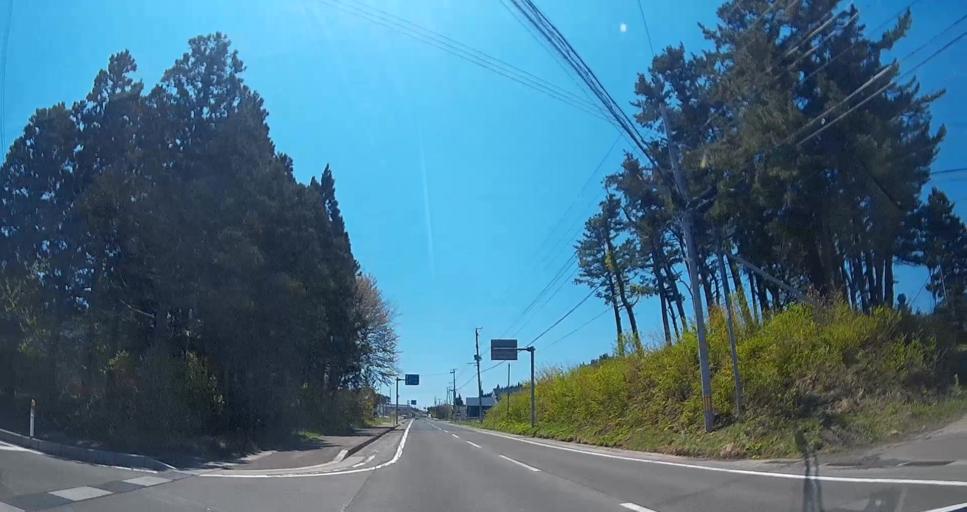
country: JP
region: Aomori
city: Mutsu
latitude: 41.0795
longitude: 141.3858
